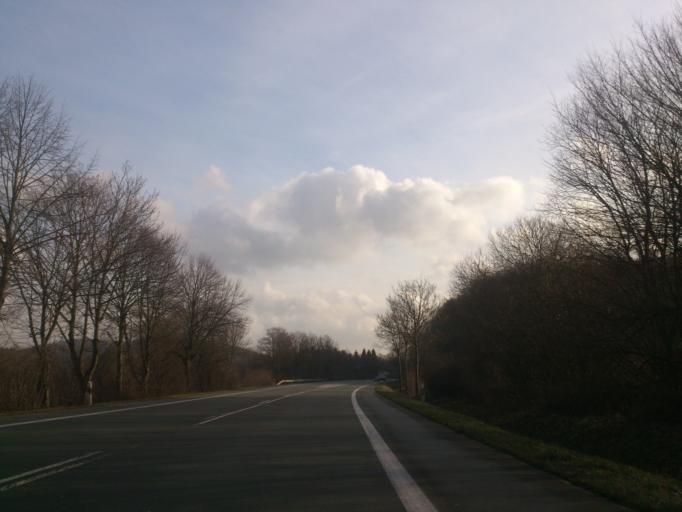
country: DE
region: North Rhine-Westphalia
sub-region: Regierungsbezirk Detmold
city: Bad Driburg
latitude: 51.7221
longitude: 9.0598
